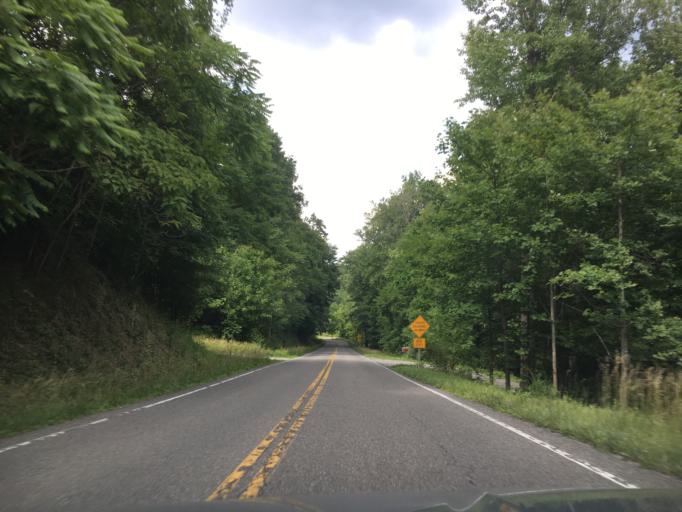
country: US
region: Virginia
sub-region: Roanoke County
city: Narrows
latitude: 37.1766
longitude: -80.0010
